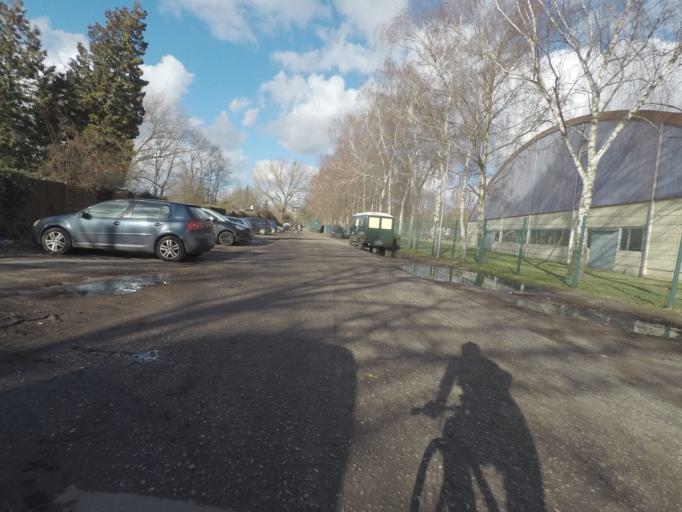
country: DE
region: Berlin
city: Bezirk Kreuzberg
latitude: 52.4829
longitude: 13.4063
